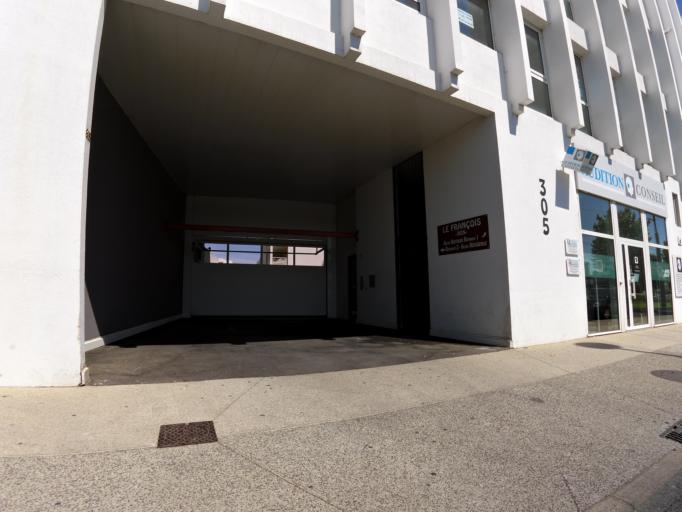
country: FR
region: Languedoc-Roussillon
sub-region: Departement de l'Herault
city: Le Cres
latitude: 43.6354
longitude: 3.9245
